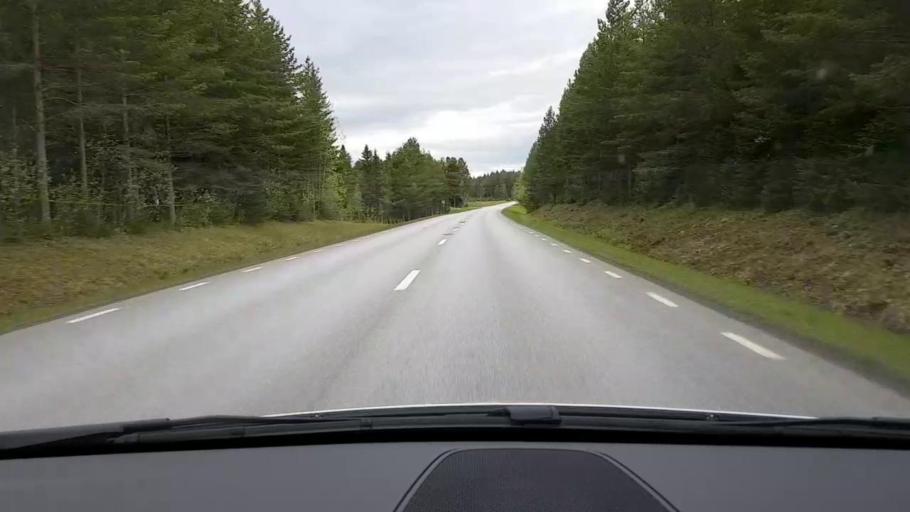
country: SE
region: Jaemtland
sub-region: Krokoms Kommun
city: Valla
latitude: 63.2736
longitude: 13.9457
